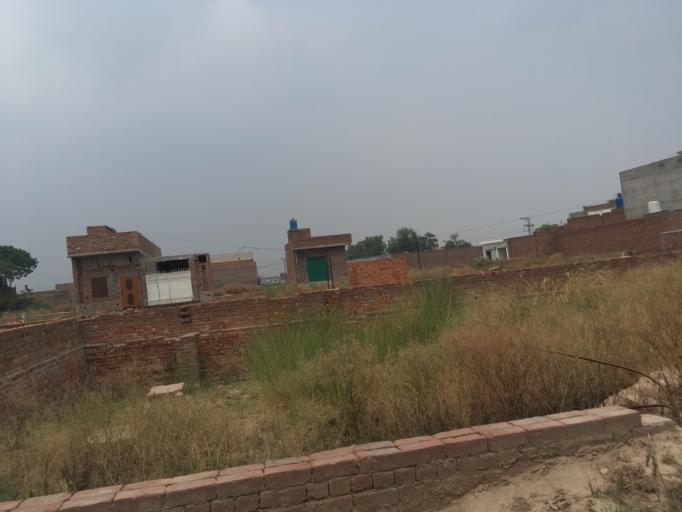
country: PK
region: Punjab
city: Lahore
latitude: 31.6124
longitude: 74.3536
